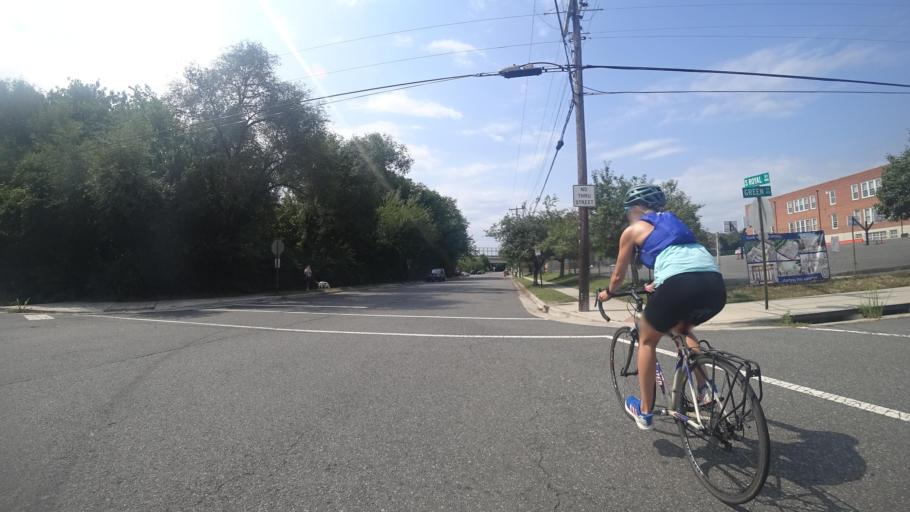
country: US
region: Virginia
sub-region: City of Alexandria
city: Alexandria
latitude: 38.7955
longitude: -77.0456
